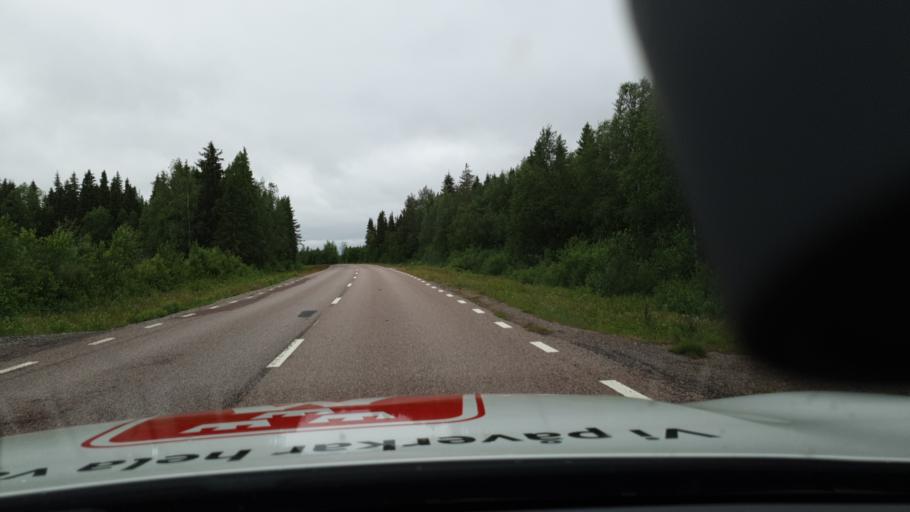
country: FI
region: Lapland
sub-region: Tunturi-Lappi
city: Kolari
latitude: 67.1043
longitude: 23.6469
